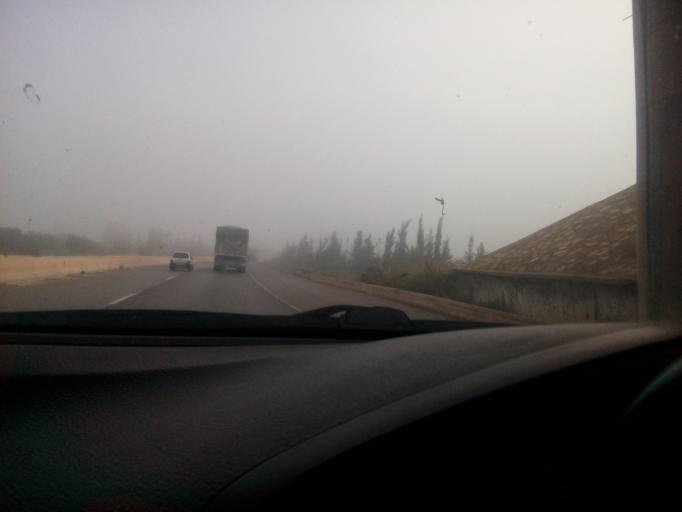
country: DZ
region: Oran
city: Mers el Kebir
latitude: 35.6073
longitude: -0.7440
